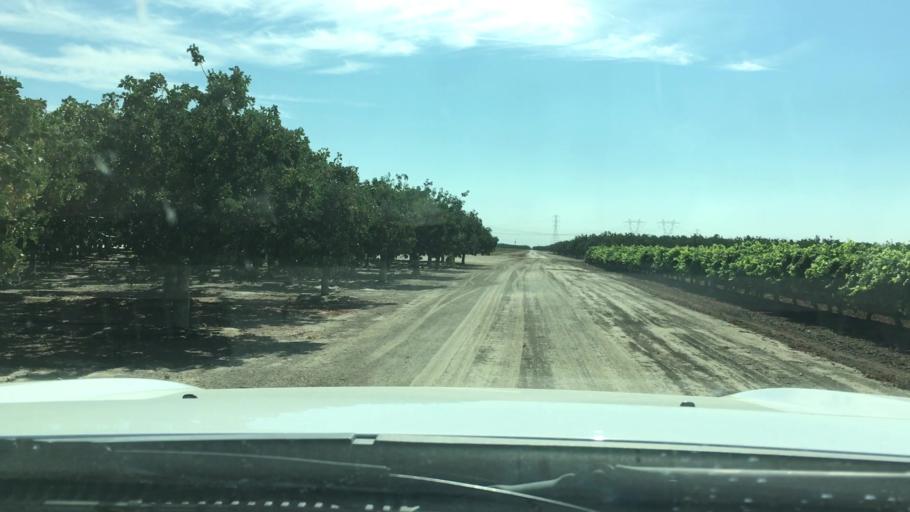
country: US
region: California
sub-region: Kern County
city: Buttonwillow
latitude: 35.3658
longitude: -119.3871
